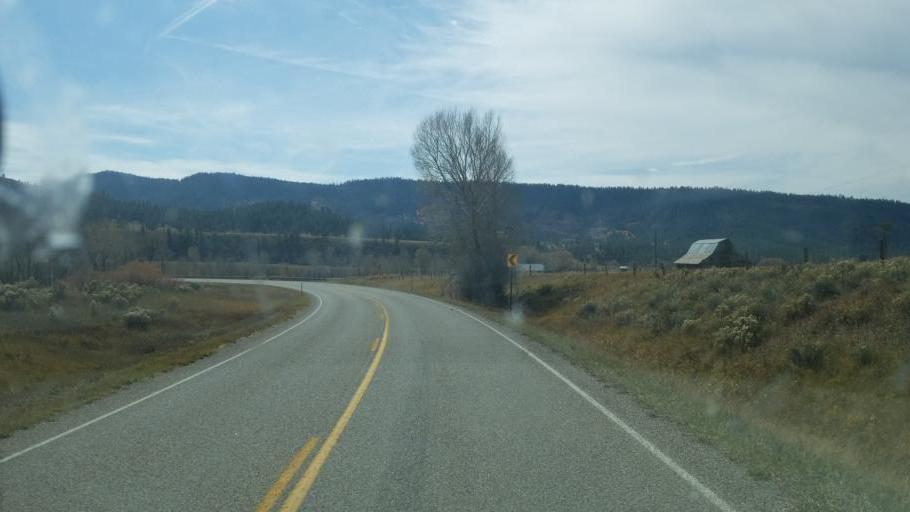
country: US
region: New Mexico
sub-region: Rio Arriba County
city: Dulce
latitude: 37.0393
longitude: -106.8445
